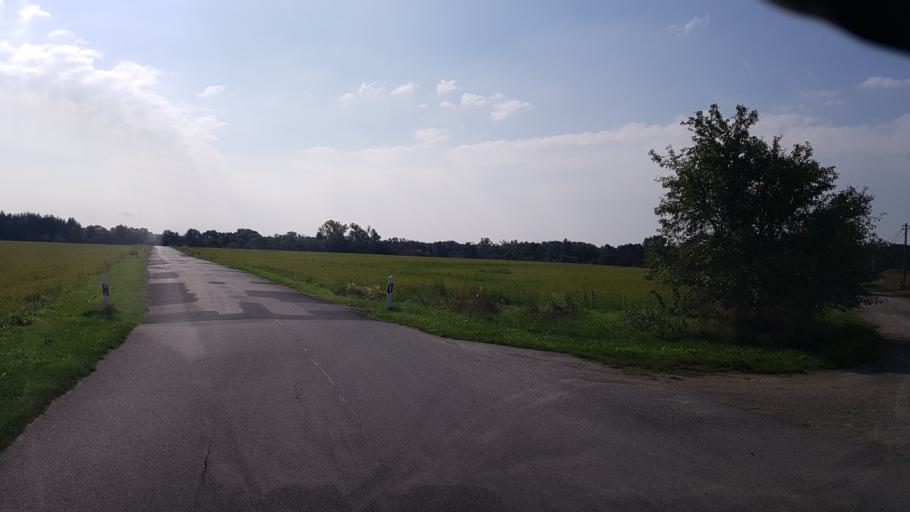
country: DE
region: Brandenburg
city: Luebben
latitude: 51.8722
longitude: 13.8518
